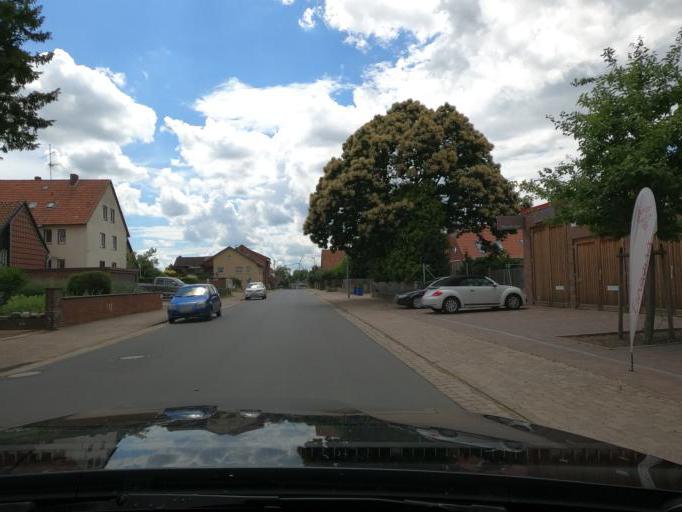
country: DE
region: Lower Saxony
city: Algermissen
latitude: 52.2719
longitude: 10.0124
